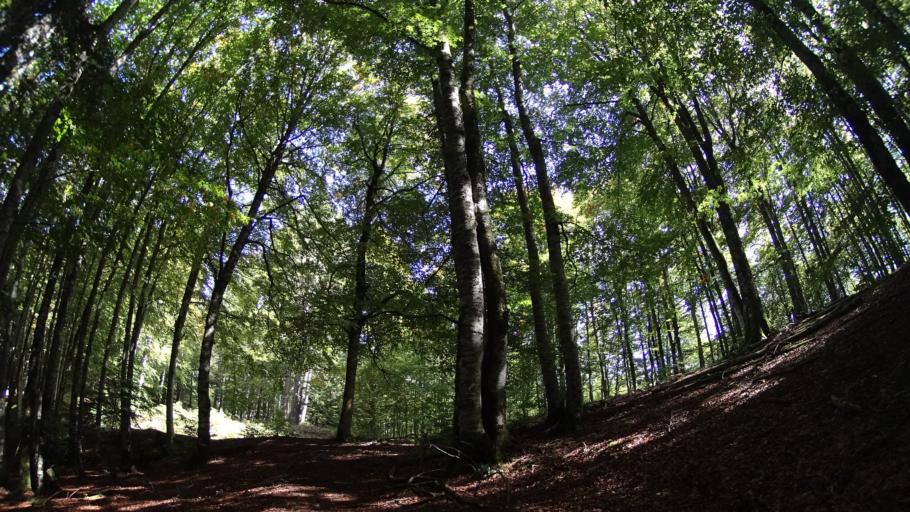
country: ES
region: Navarre
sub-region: Provincia de Navarra
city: Orbara
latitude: 42.9897
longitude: -1.1329
